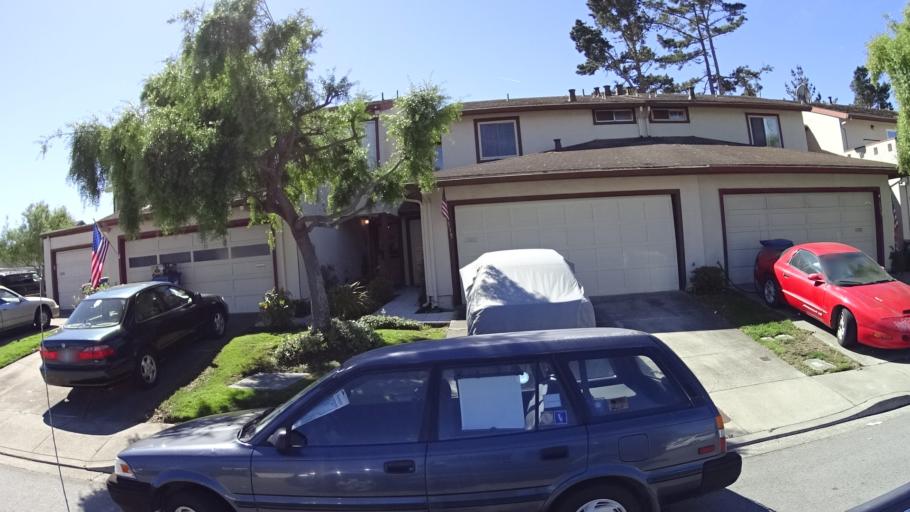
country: US
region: California
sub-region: San Mateo County
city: Broadmoor
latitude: 37.6821
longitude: -122.4794
